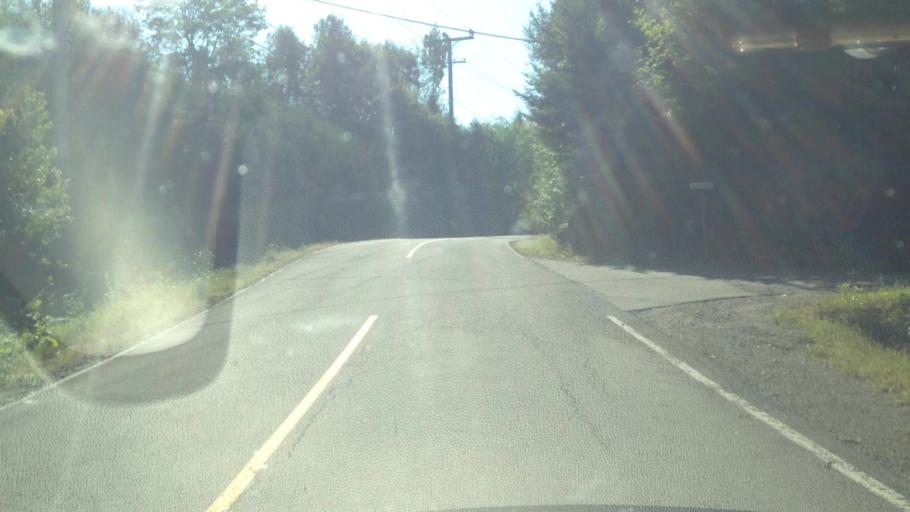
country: CA
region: Quebec
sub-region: Laurentides
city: Prevost
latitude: 45.9071
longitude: -74.0078
